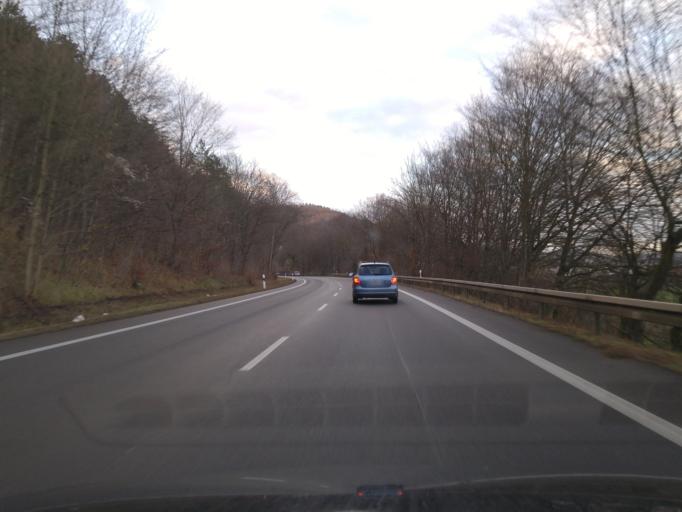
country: DE
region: Hesse
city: Witzenhausen
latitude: 51.3571
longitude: 9.8380
